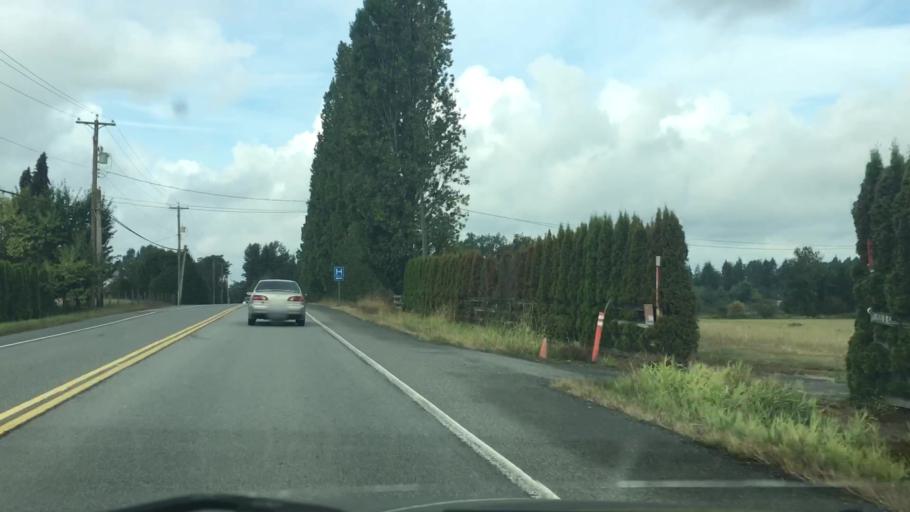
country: CA
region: British Columbia
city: Langley
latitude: 49.1045
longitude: -122.6009
